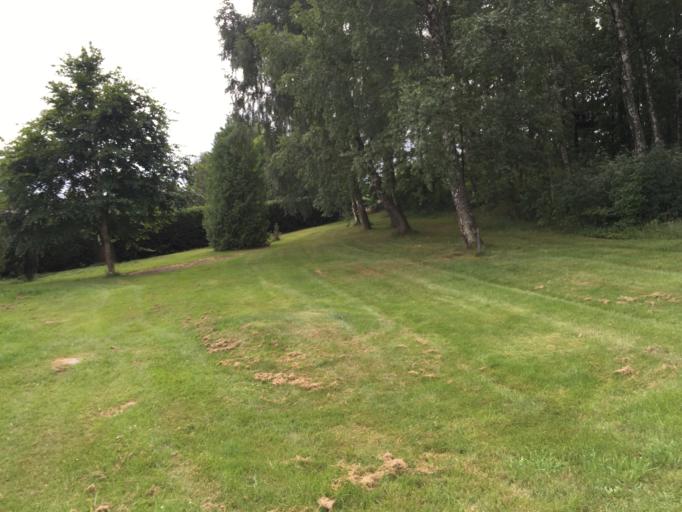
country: SE
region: Halland
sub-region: Laholms Kommun
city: Veinge
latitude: 56.5509
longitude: 13.0685
